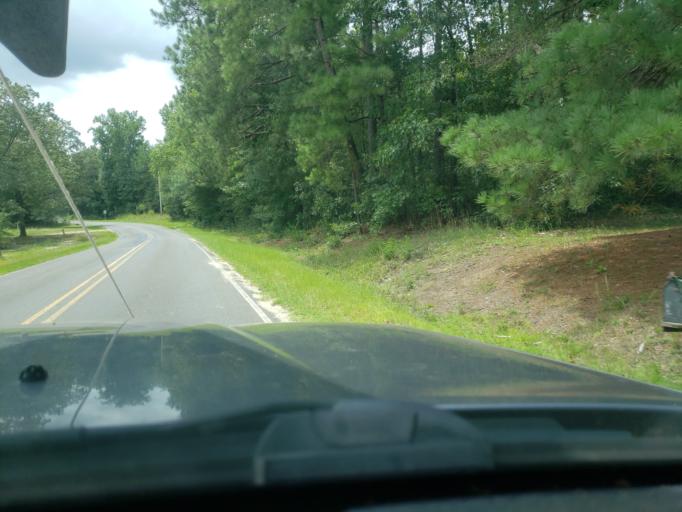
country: US
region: North Carolina
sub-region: Wake County
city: Zebulon
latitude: 35.8930
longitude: -78.3408
